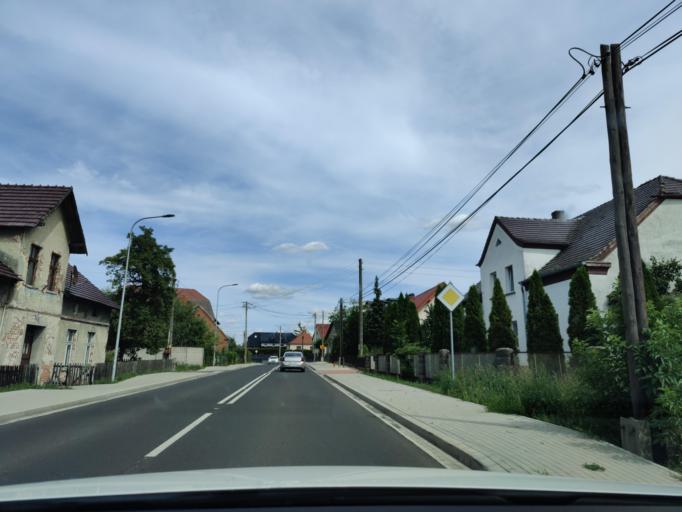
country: PL
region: Opole Voivodeship
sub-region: Powiat krapkowicki
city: Strzeleczki
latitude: 50.4407
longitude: 17.7970
